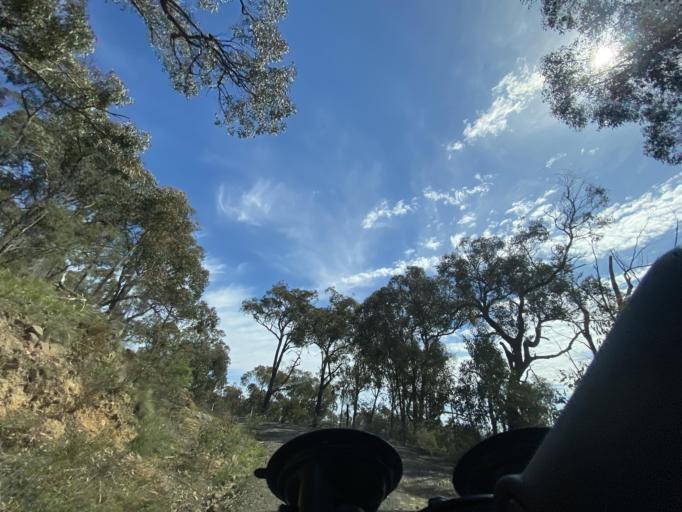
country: AU
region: Victoria
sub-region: Mansfield
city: Mansfield
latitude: -36.8082
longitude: 146.1031
